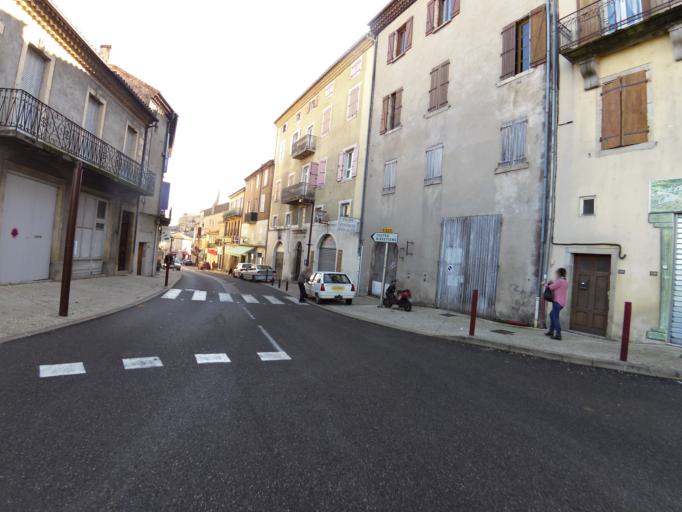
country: FR
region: Rhone-Alpes
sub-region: Departement de l'Ardeche
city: Joyeuse
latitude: 44.4800
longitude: 4.2360
